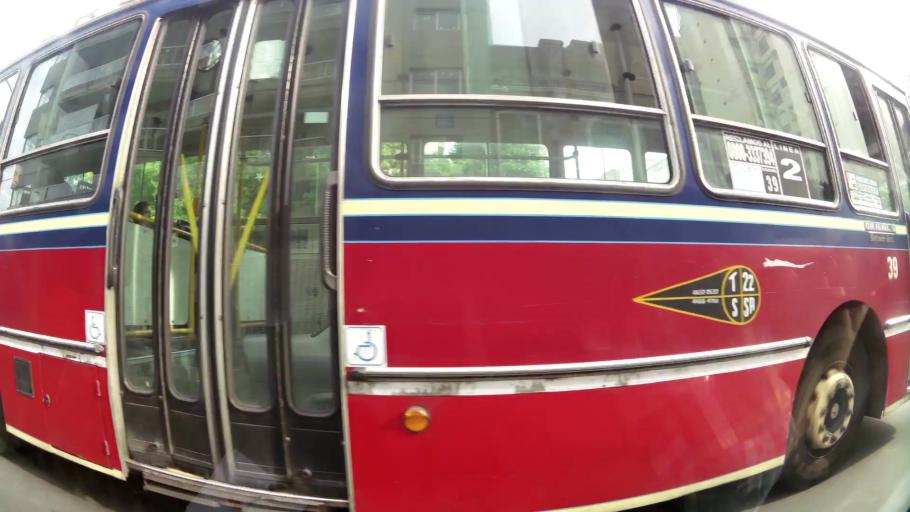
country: AR
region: Buenos Aires F.D.
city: Villa Santa Rita
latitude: -34.6327
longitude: -58.4771
